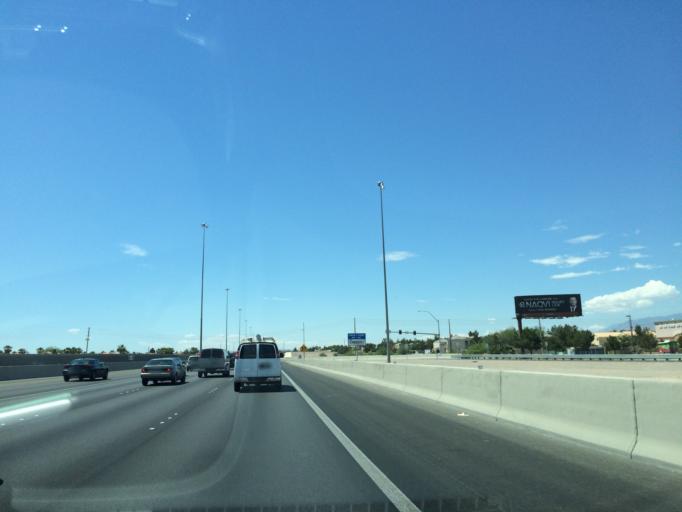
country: US
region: Nevada
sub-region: Clark County
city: Las Vegas
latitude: 36.2393
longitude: -115.2471
